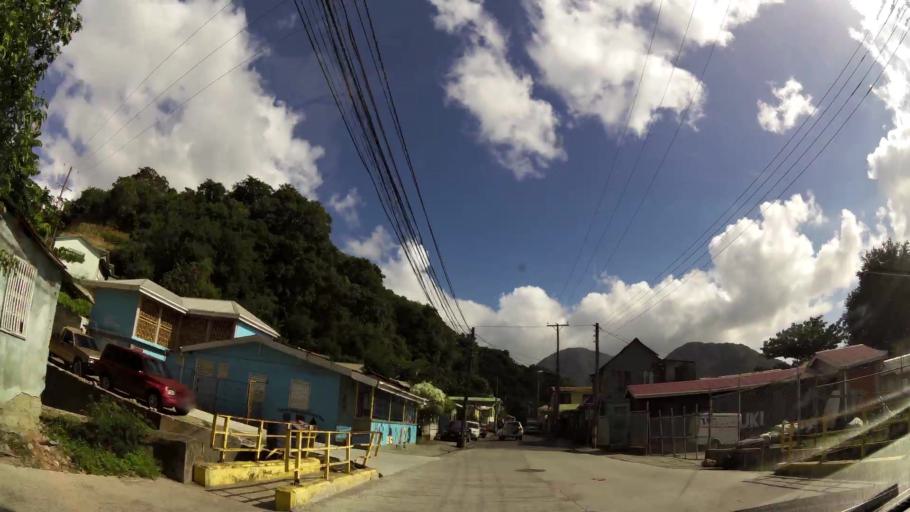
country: DM
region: Saint George
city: Roseau
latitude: 15.2917
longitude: -61.3790
